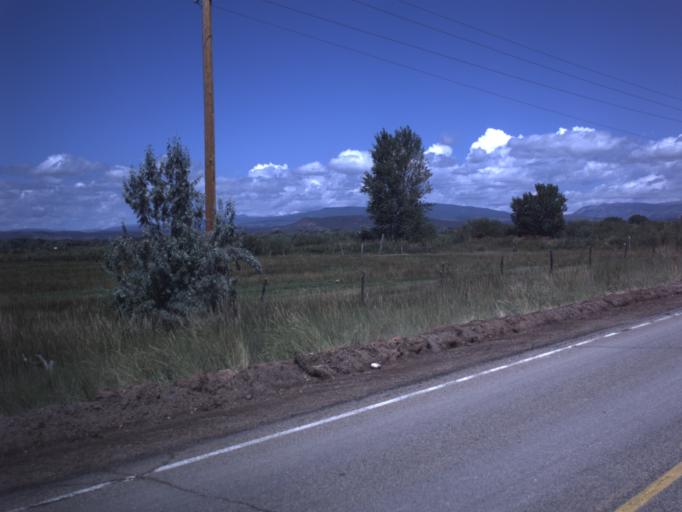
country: US
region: Utah
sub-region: Duchesne County
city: Roosevelt
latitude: 40.4172
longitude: -110.0299
